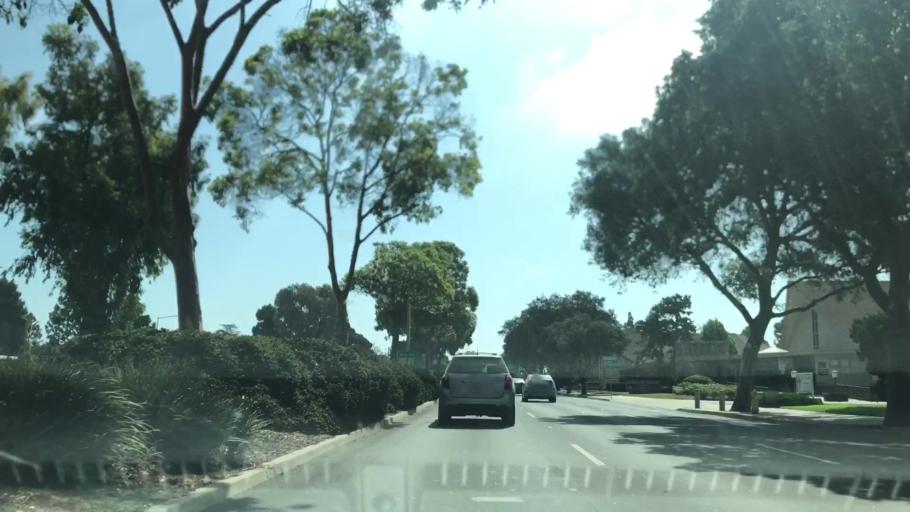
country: US
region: California
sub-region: Ventura County
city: El Rio
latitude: 34.2659
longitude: -119.2086
